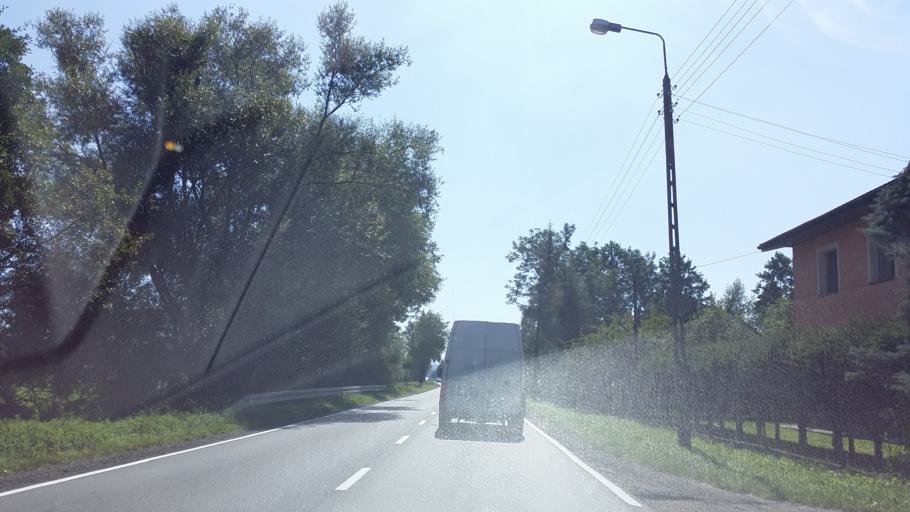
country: PL
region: Lesser Poland Voivodeship
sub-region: Powiat oswiecimski
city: Zator
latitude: 49.9803
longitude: 19.4387
